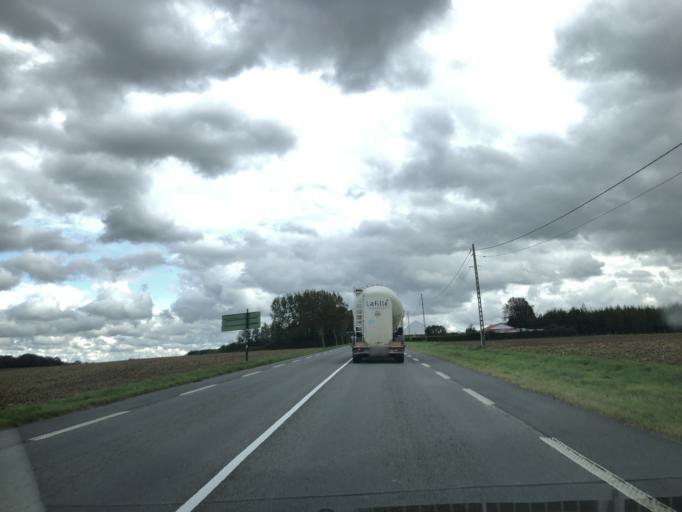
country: FR
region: Nord-Pas-de-Calais
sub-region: Departement du Pas-de-Calais
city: Fruges
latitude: 50.5381
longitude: 2.1086
